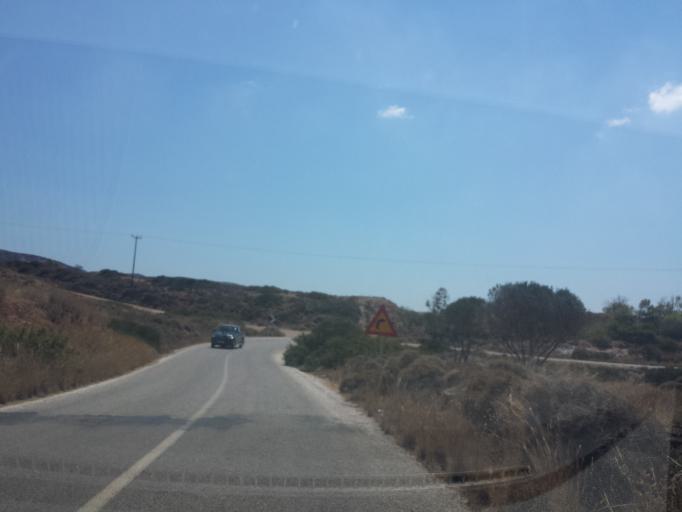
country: GR
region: South Aegean
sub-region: Nomos Kykladon
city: Adamas
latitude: 36.6838
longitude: 24.5070
